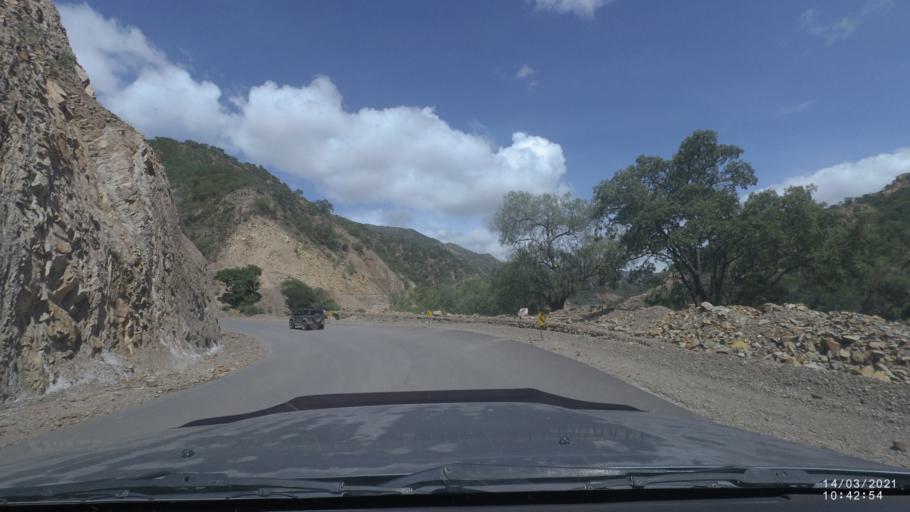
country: BO
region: Cochabamba
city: Tarata
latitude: -17.8780
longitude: -65.9216
